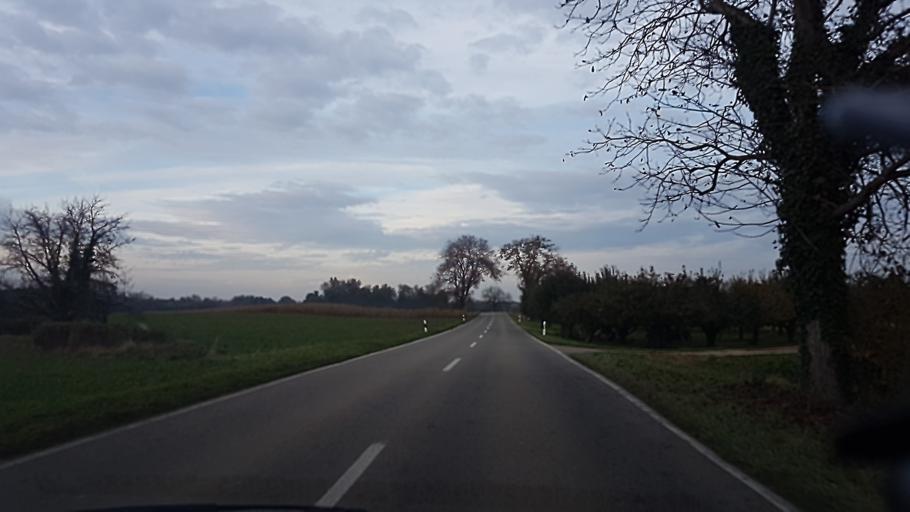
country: DE
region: Baden-Wuerttemberg
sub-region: Freiburg Region
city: Wyhl
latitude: 48.1795
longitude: 7.6642
